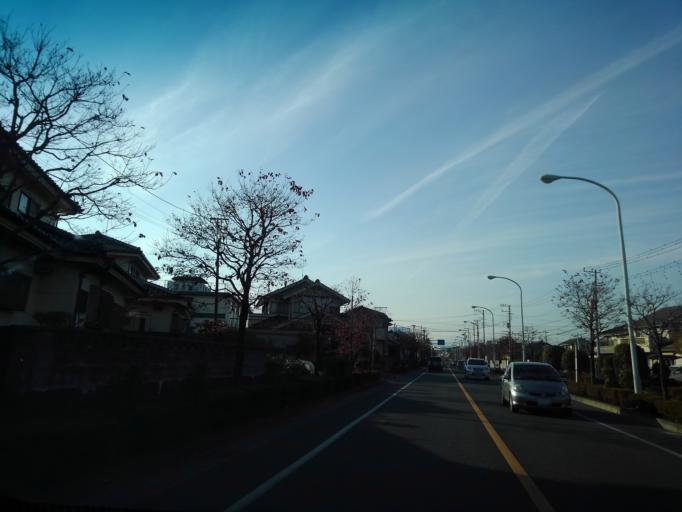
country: JP
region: Tokyo
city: Fussa
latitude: 35.7916
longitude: 139.3587
